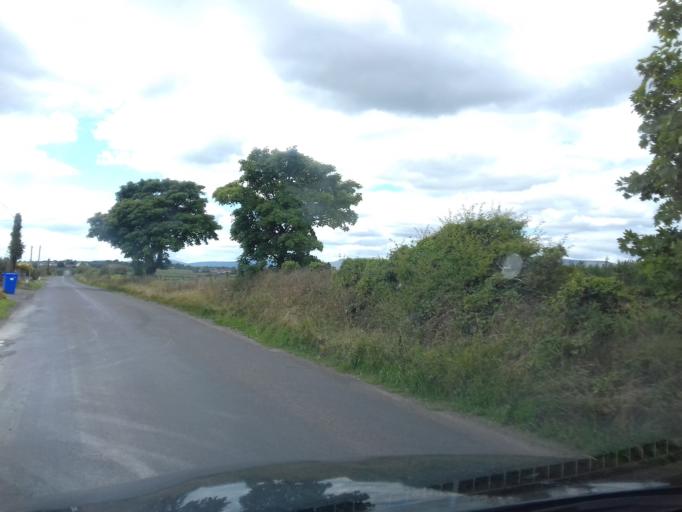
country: IE
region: Munster
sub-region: Waterford
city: Portlaw
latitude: 52.1799
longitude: -7.3124
